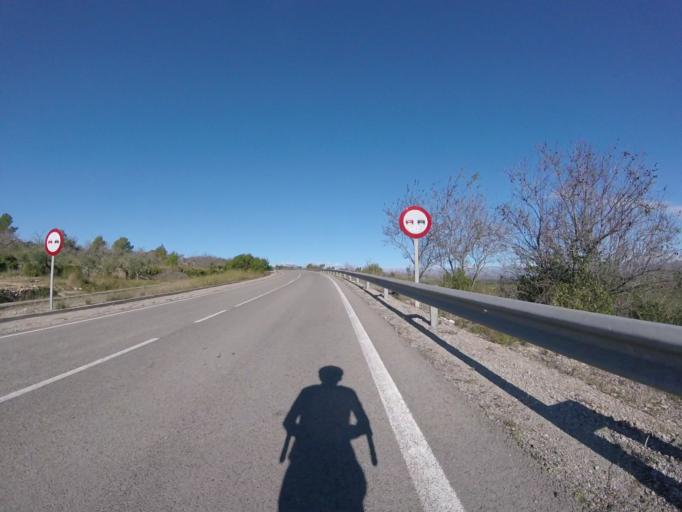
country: ES
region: Valencia
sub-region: Provincia de Castello
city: Cervera del Maestre
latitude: 40.4717
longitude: 0.2406
